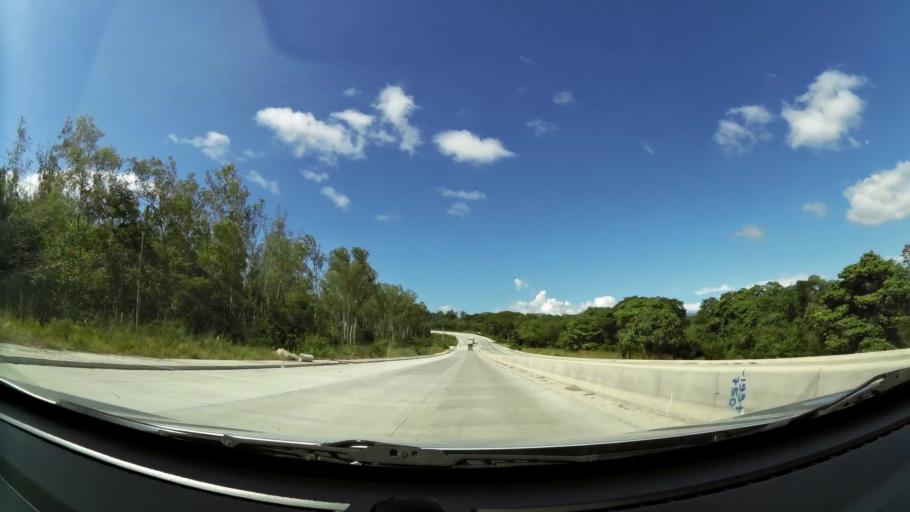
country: CR
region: Guanacaste
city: Bagaces
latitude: 10.5327
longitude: -85.2873
